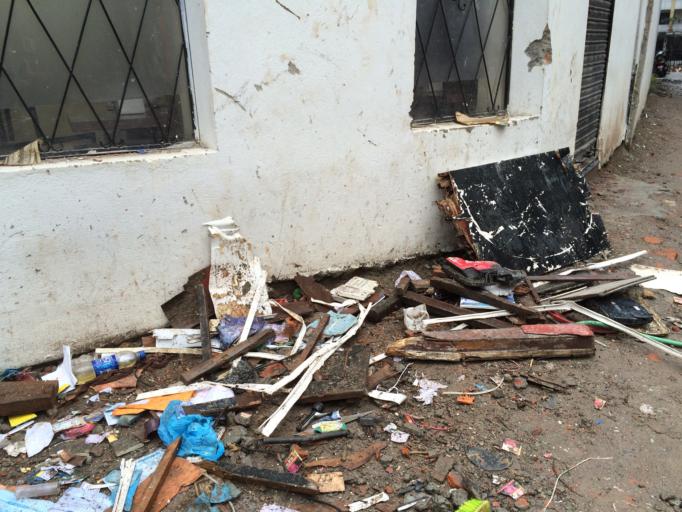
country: NP
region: Central Region
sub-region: Bagmati Zone
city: Kathmandu
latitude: 27.7173
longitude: 85.3127
